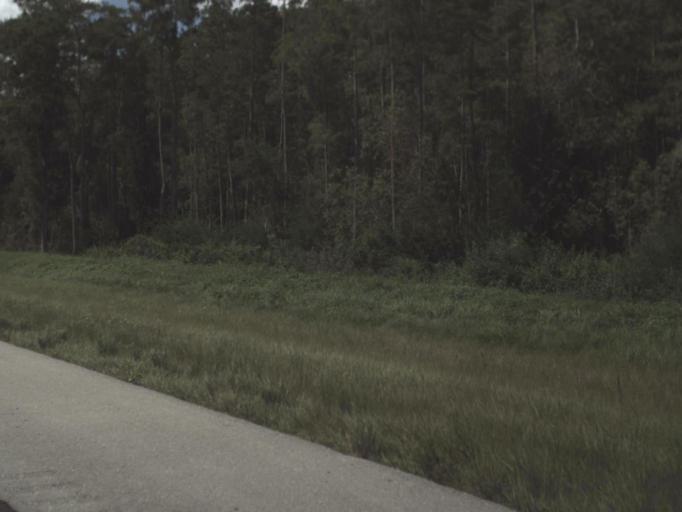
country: US
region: Florida
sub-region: Lee County
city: Gateway
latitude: 26.5676
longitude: -81.7938
